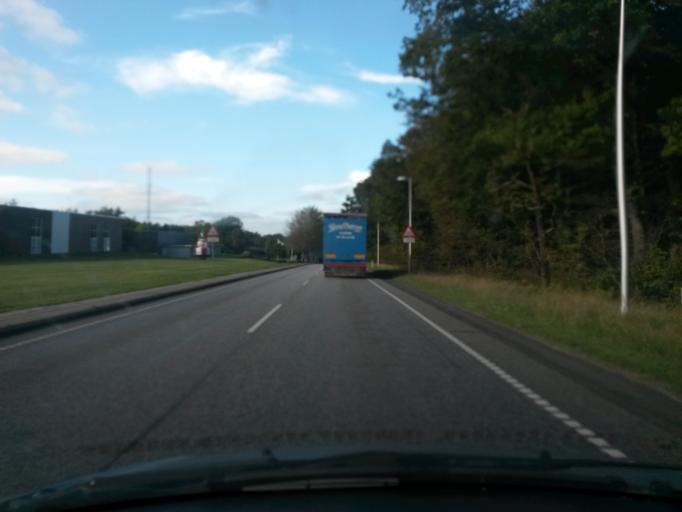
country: DK
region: Central Jutland
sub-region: Holstebro Kommune
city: Holstebro
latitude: 56.3424
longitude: 8.6368
